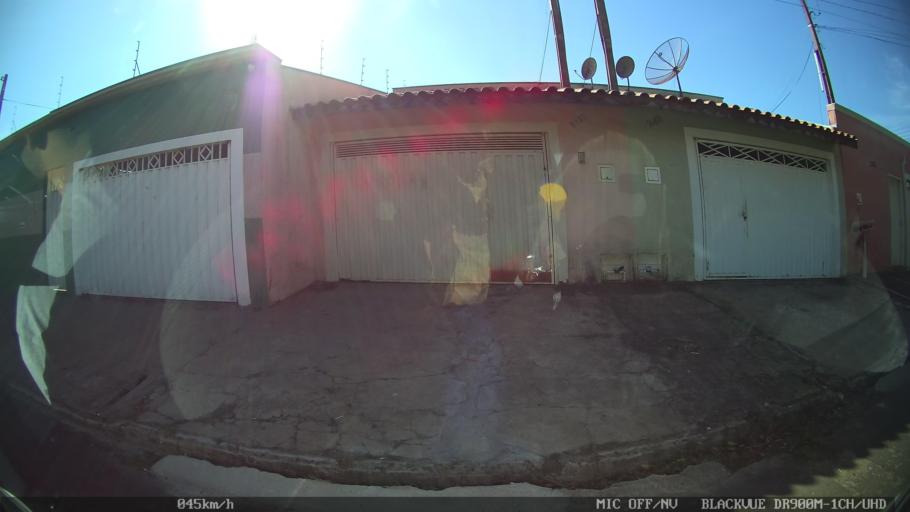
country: BR
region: Sao Paulo
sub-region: Franca
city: Franca
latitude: -20.4912
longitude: -47.4248
